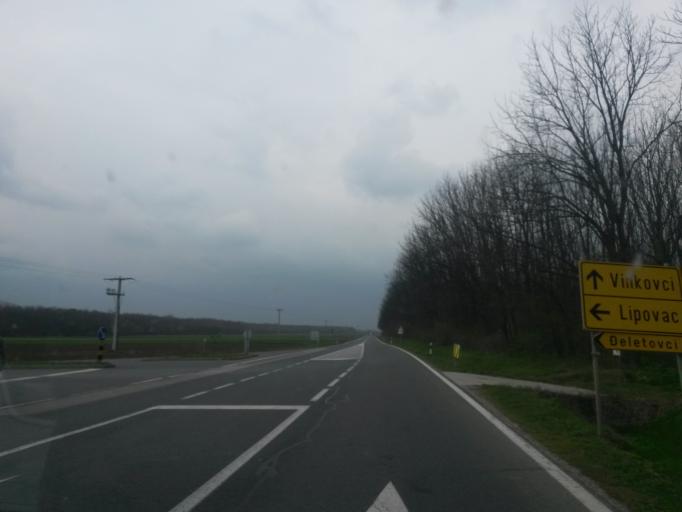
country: HR
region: Vukovarsko-Srijemska
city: Nijemci
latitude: 45.1975
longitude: 19.0227
